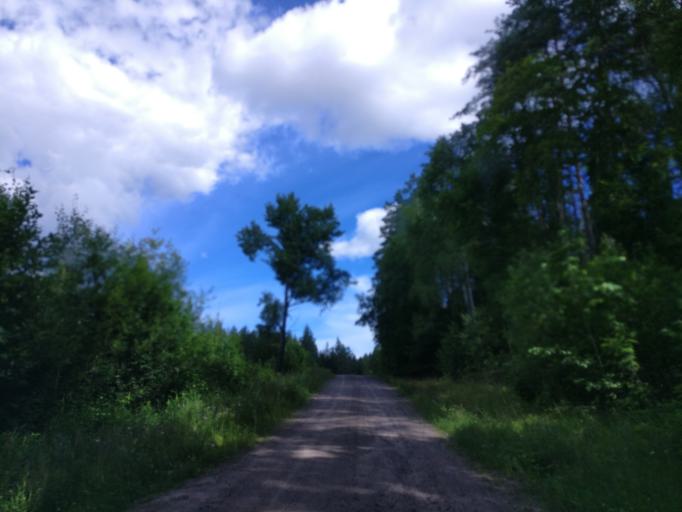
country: SE
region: Vaermland
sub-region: Hagfors Kommun
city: Hagfors
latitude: 60.0345
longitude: 13.5365
